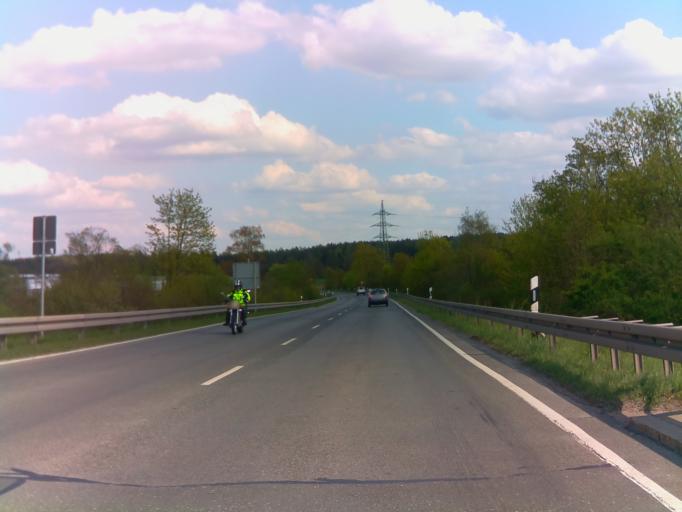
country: DE
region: Bavaria
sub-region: Upper Franconia
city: Neustadt bei Coburg
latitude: 50.3119
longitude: 11.1008
